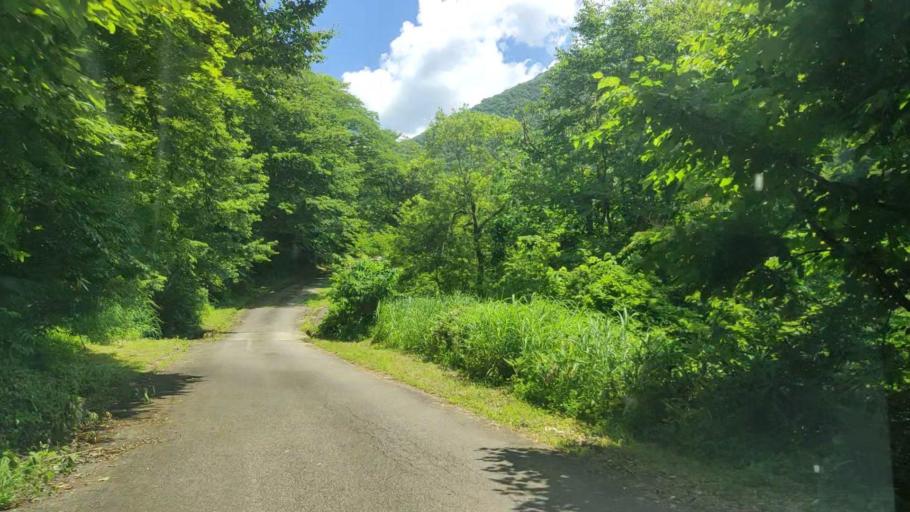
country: JP
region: Fukui
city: Ono
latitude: 35.7897
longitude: 136.5042
